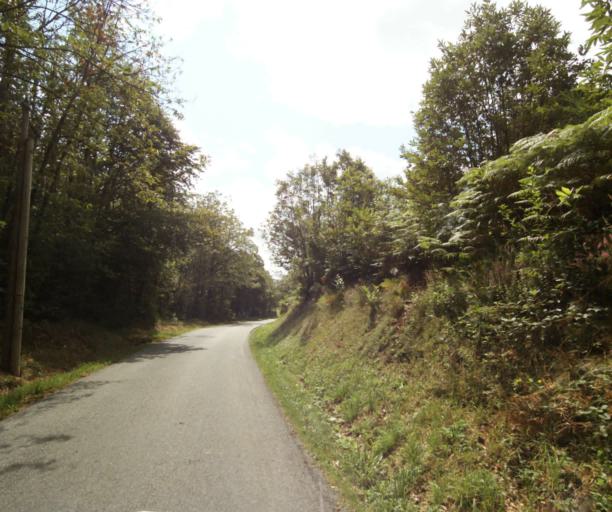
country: FR
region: Limousin
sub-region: Departement de la Correze
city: Sainte-Fortunade
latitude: 45.1783
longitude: 1.7979
